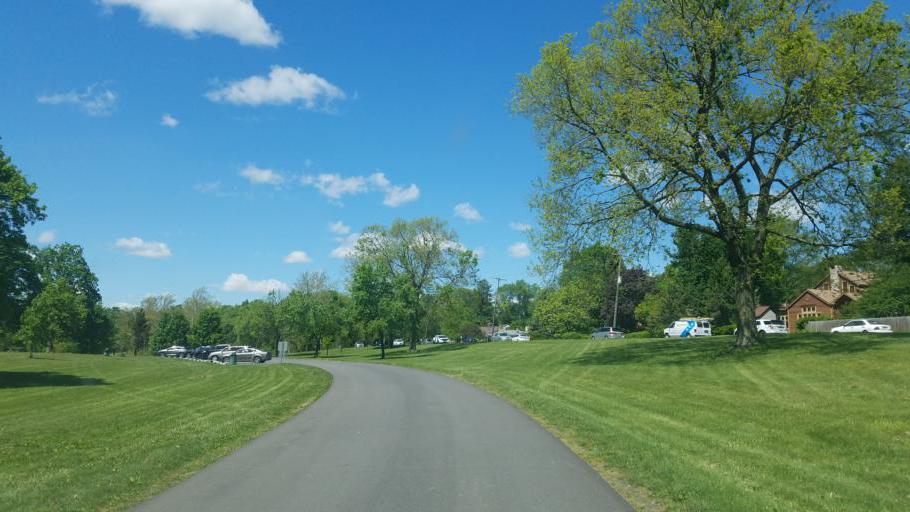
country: US
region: Ohio
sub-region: Franklin County
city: Upper Arlington
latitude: 40.0336
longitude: -83.0932
